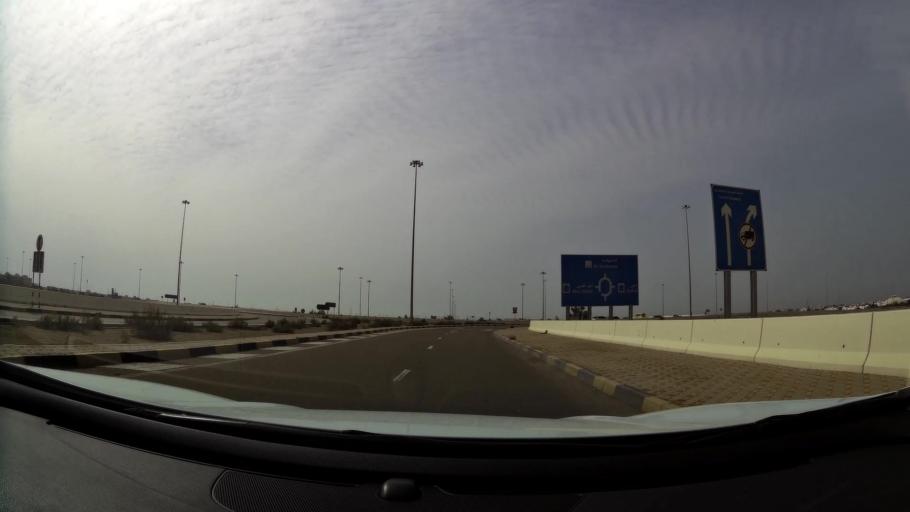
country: AE
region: Abu Dhabi
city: Abu Dhabi
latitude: 24.5639
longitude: 54.6980
